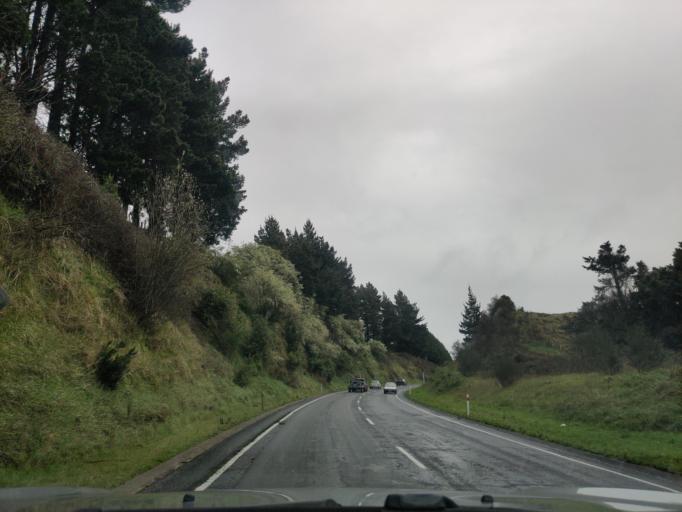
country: NZ
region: Manawatu-Wanganui
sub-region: Palmerston North City
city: Palmerston North
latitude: -40.0542
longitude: 176.2379
